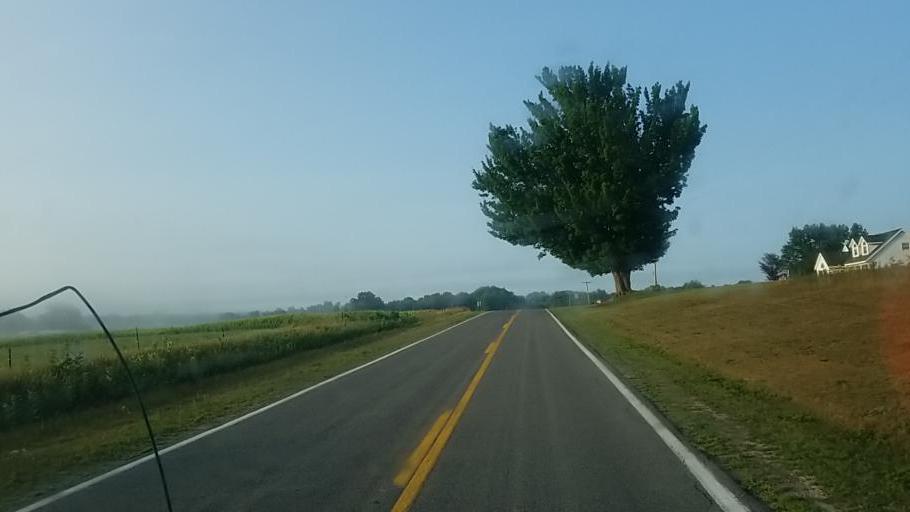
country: US
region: Michigan
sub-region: Muskegon County
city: Twin Lake
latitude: 43.4433
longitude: -86.0792
